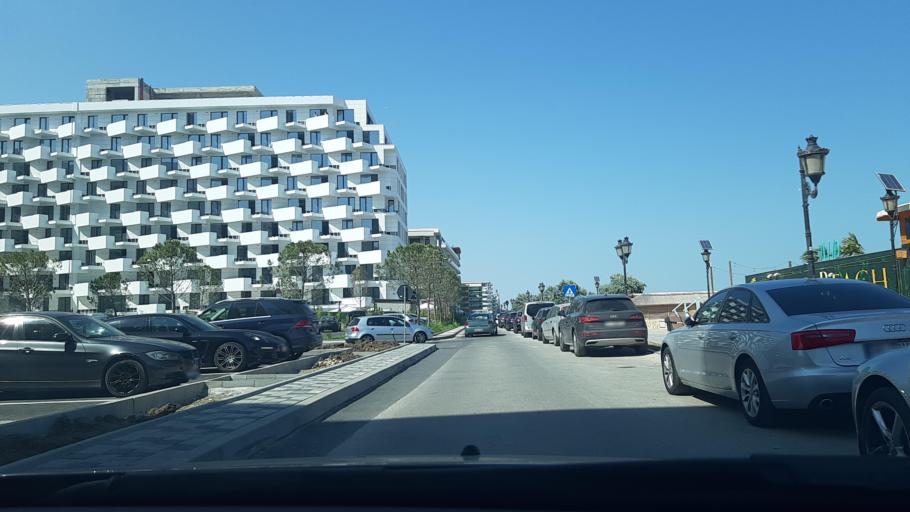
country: RO
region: Constanta
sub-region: Comuna Navodari
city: Navodari
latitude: 44.3053
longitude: 28.6280
